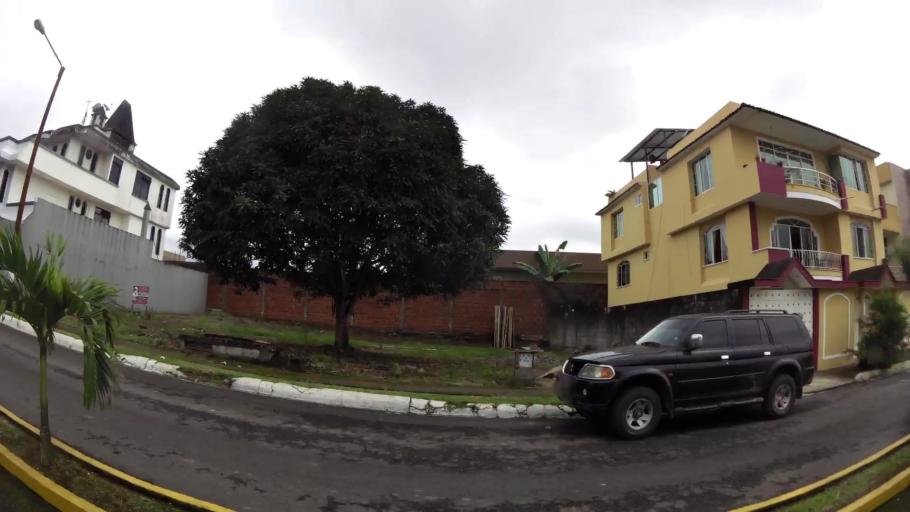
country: EC
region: Santo Domingo de los Tsachilas
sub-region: Canton Santo Domingo de los Colorados
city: Santo Domingo de los Colorados
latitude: -0.2538
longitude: -79.1552
